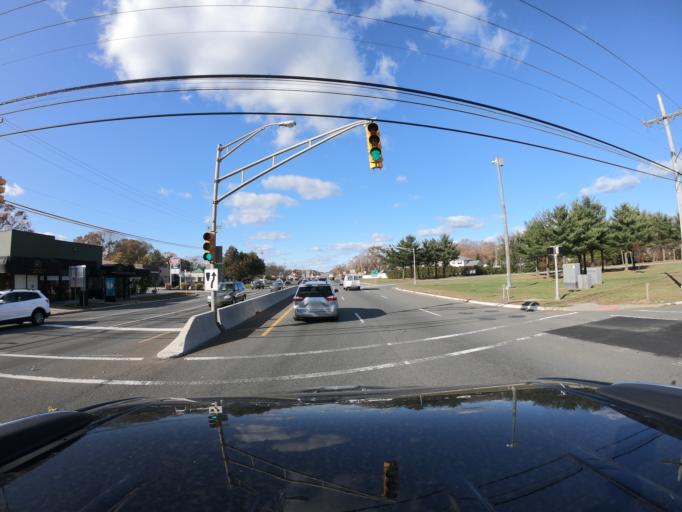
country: US
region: New Jersey
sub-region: Ocean County
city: Lakewood
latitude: 40.1553
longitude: -74.2297
